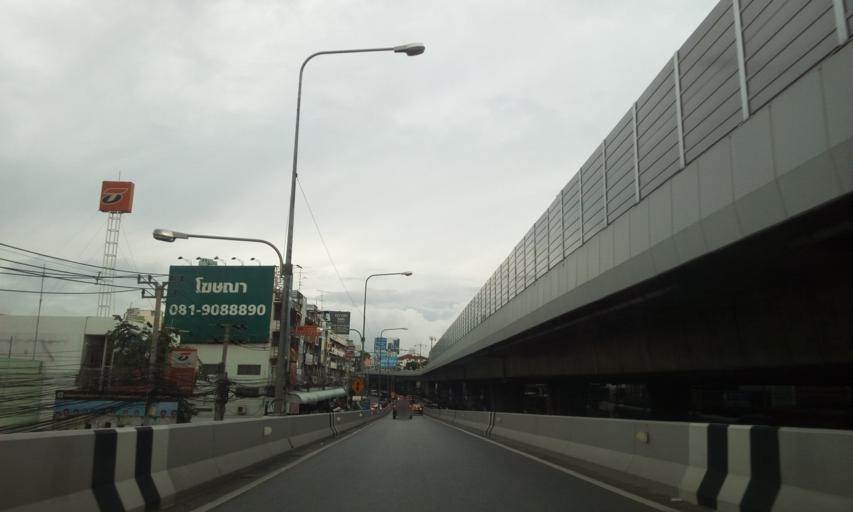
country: TH
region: Nonthaburi
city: Pak Kret
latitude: 13.9122
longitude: 100.4975
